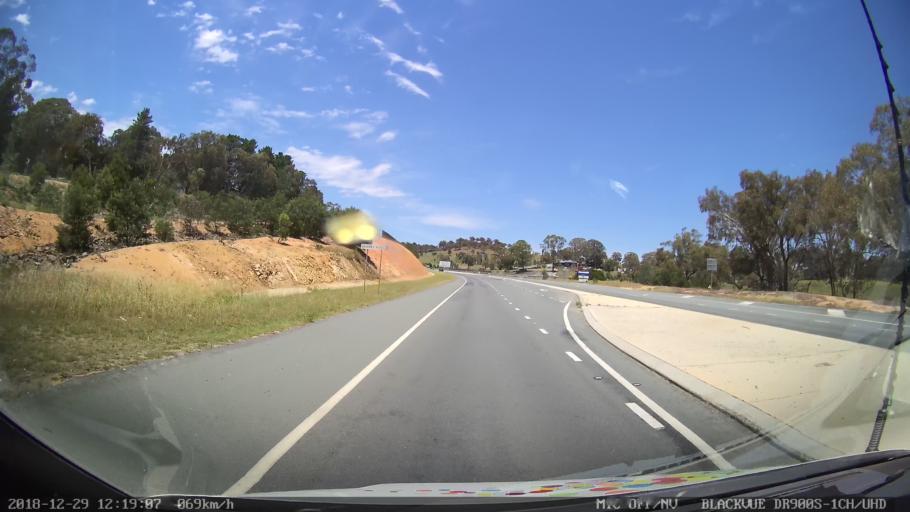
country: AU
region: New South Wales
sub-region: Queanbeyan
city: Queanbeyan
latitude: -35.3906
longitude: 149.2341
